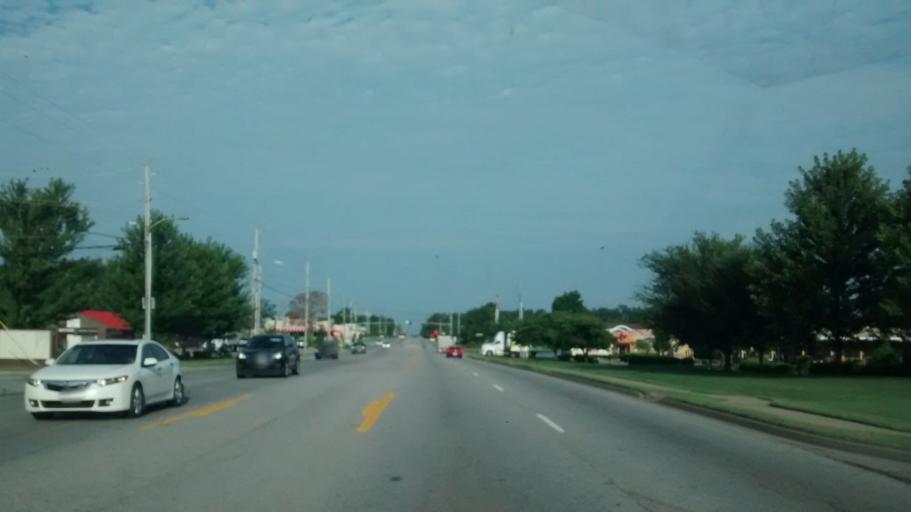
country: US
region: Arkansas
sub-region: Washington County
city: Fayetteville
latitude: 36.0784
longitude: -94.2049
